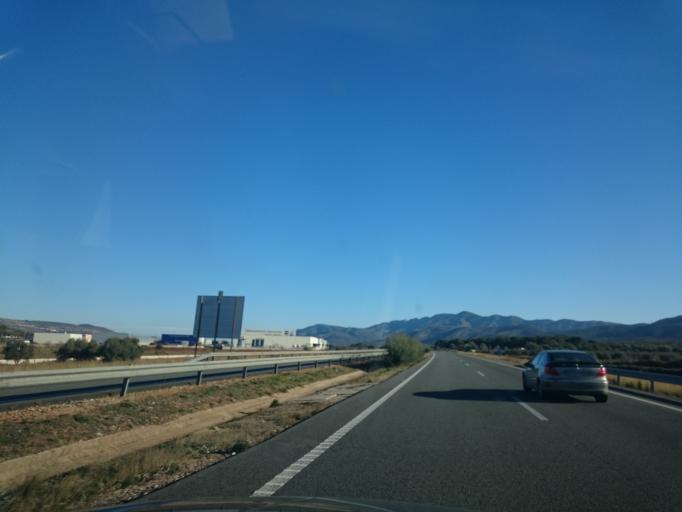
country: ES
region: Catalonia
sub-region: Provincia de Tarragona
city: Ulldecona
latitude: 40.5758
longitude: 0.4450
